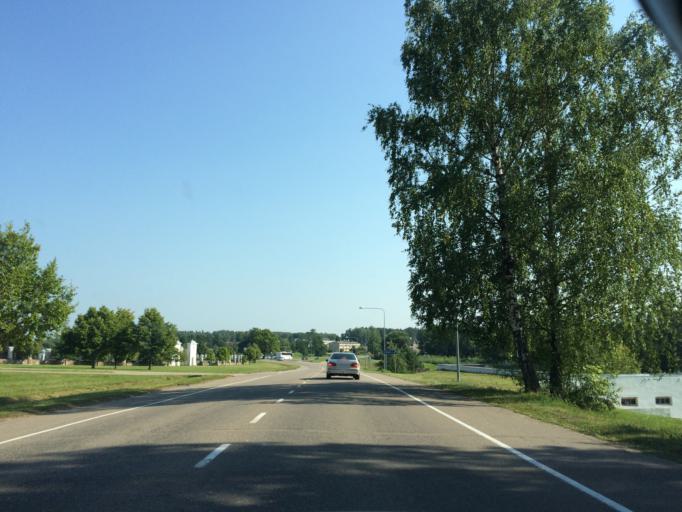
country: LV
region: Aglona
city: Aglona
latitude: 56.1278
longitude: 27.0100
